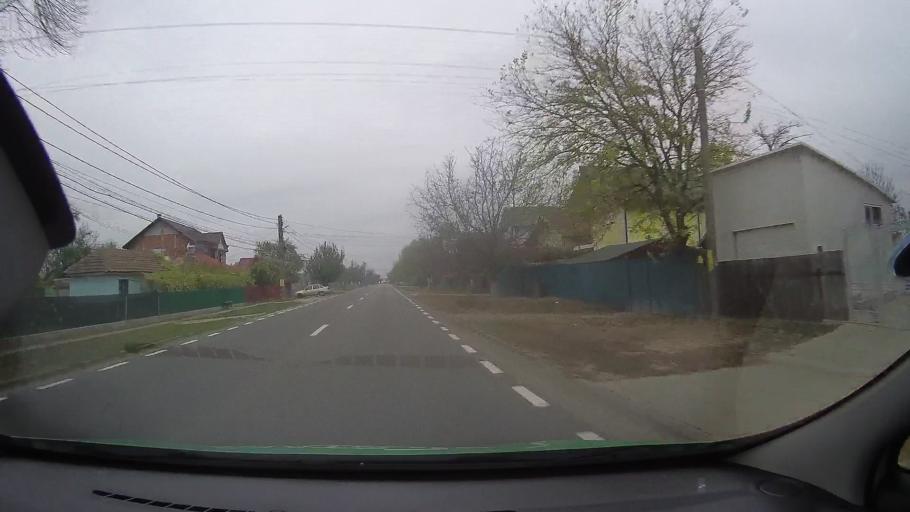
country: RO
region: Ialomita
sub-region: Comuna Slobozia
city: Slobozia
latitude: 44.6006
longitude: 27.3884
